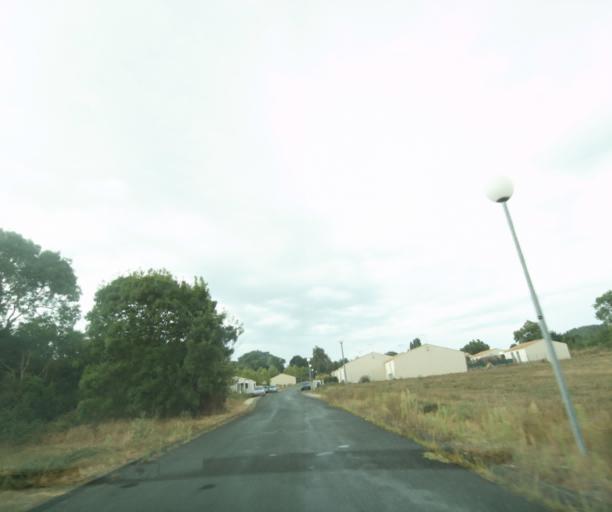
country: FR
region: Poitou-Charentes
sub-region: Departement de la Charente-Maritime
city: Tonnay-Charente
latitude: 45.9444
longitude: -0.8776
